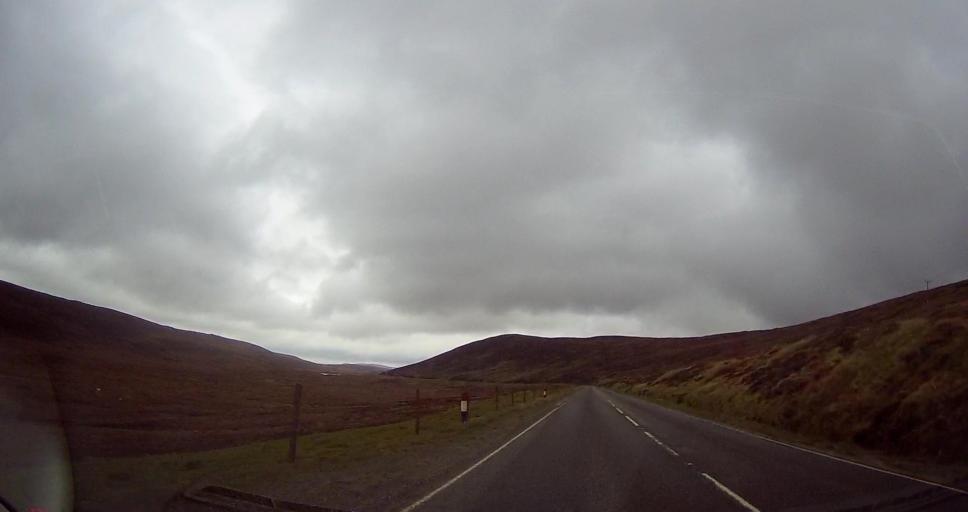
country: GB
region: Scotland
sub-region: Shetland Islands
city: Lerwick
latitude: 60.2970
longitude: -1.2395
